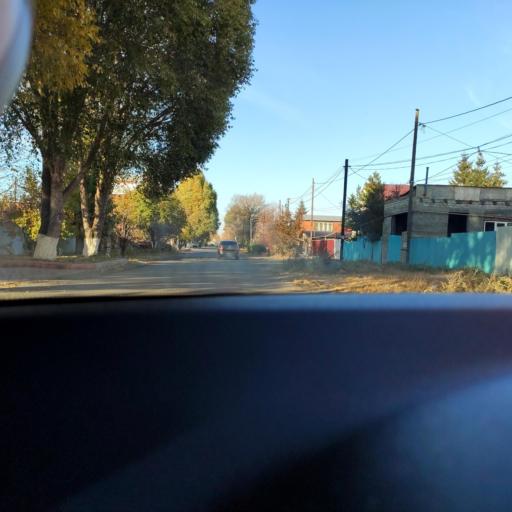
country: RU
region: Samara
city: Petra-Dubrava
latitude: 53.2513
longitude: 50.3286
